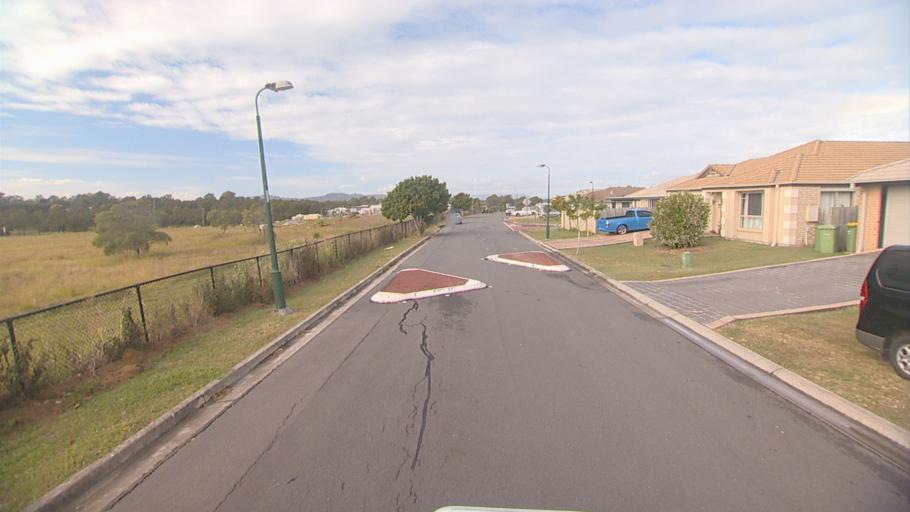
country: AU
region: Queensland
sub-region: Logan
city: Waterford West
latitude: -27.6949
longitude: 153.1154
